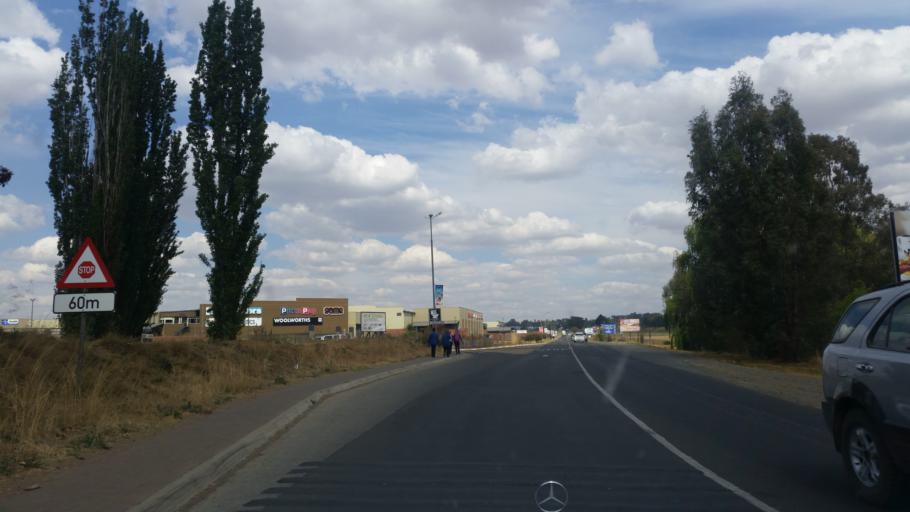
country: ZA
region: Orange Free State
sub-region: Thabo Mofutsanyana District Municipality
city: Bethlehem
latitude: -28.2405
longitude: 28.3231
